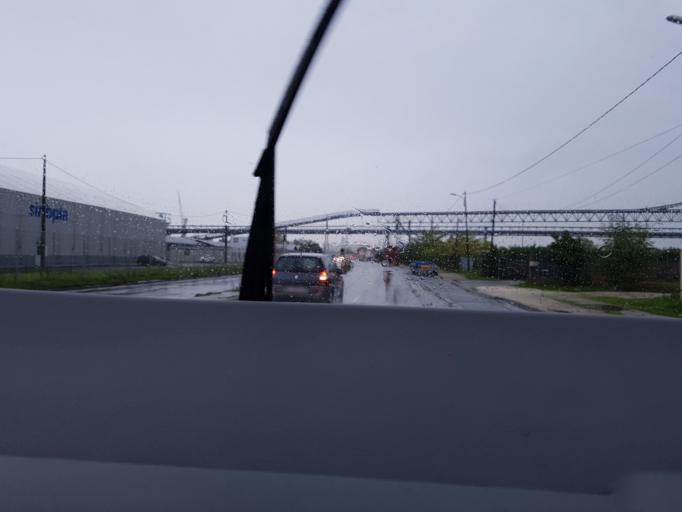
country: FR
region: Aquitaine
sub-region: Departement de la Gironde
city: Bassens
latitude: 44.8956
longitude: -0.5306
